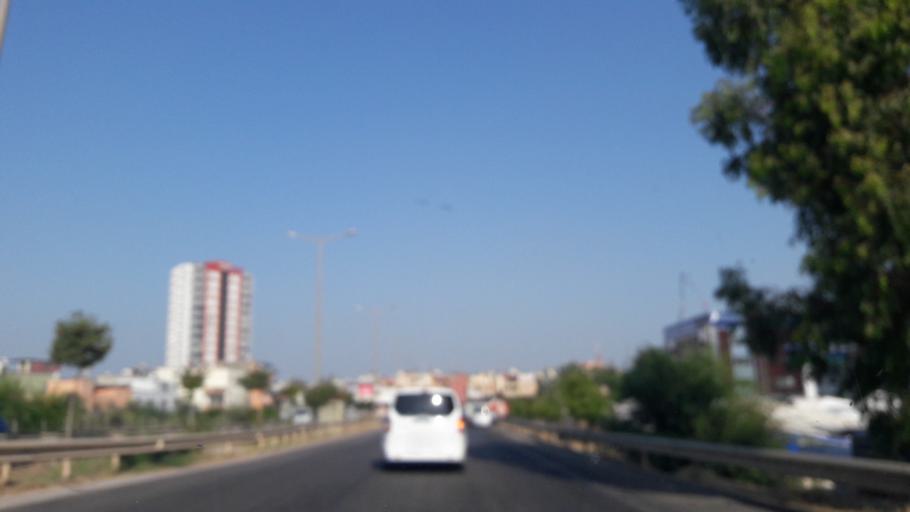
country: TR
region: Adana
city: Yuregir
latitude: 37.0237
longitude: 35.4009
